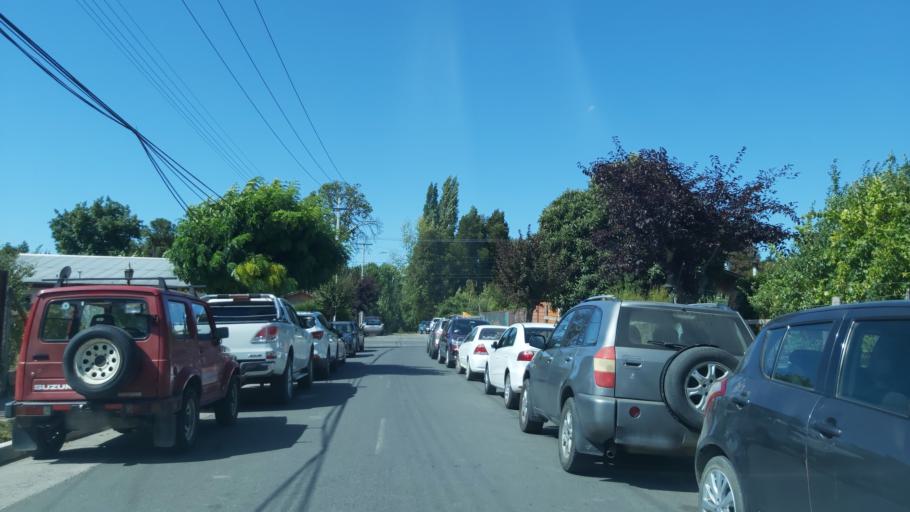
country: CL
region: Biobio
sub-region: Provincia de Concepcion
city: Lota
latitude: -37.1736
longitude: -72.9373
